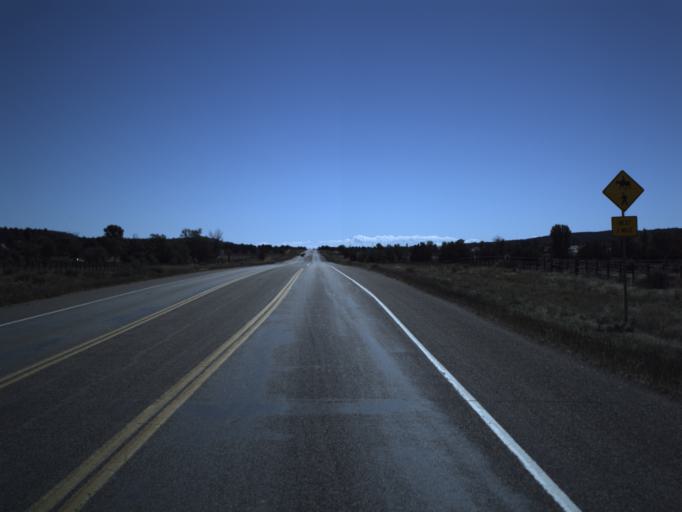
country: US
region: Utah
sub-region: Washington County
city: Ivins
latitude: 37.3076
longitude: -113.6722
